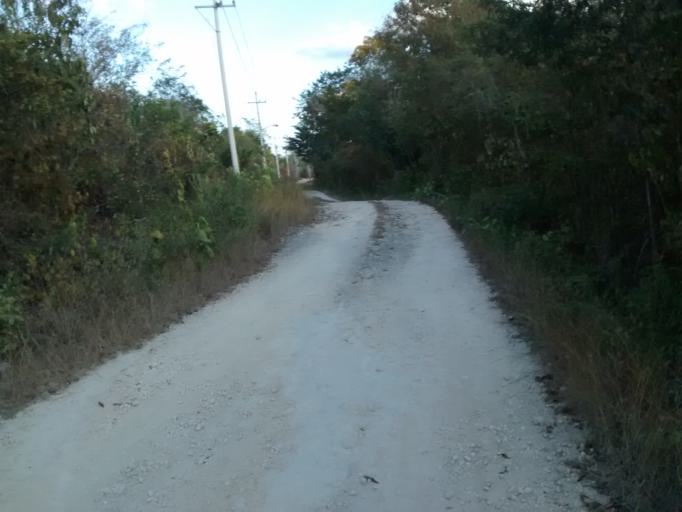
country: MX
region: Yucatan
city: Chichimila
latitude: 20.4473
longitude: -88.1997
